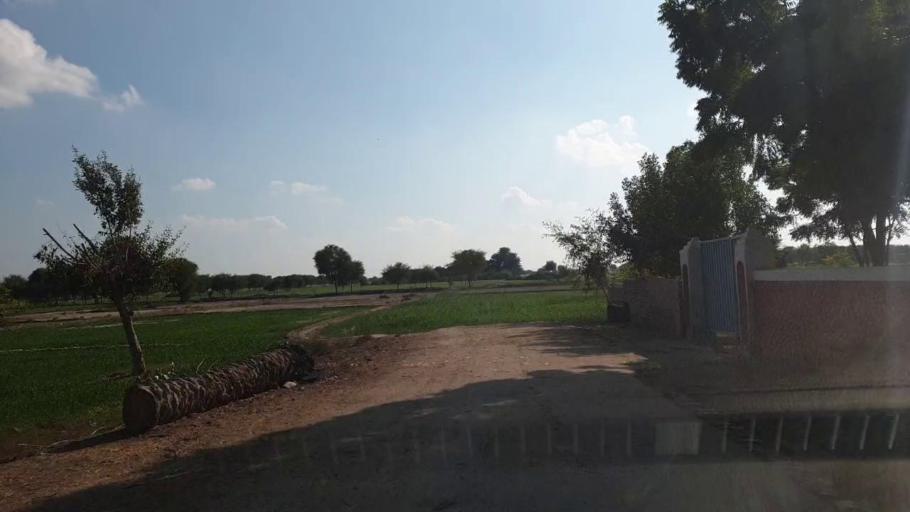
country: PK
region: Sindh
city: Shahpur Chakar
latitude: 26.1093
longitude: 68.5548
